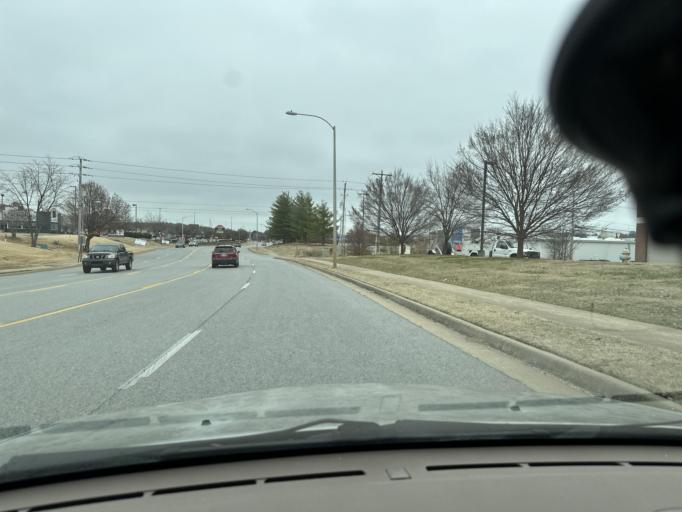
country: US
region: Arkansas
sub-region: Washington County
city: Johnson
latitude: 36.1241
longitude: -94.1544
